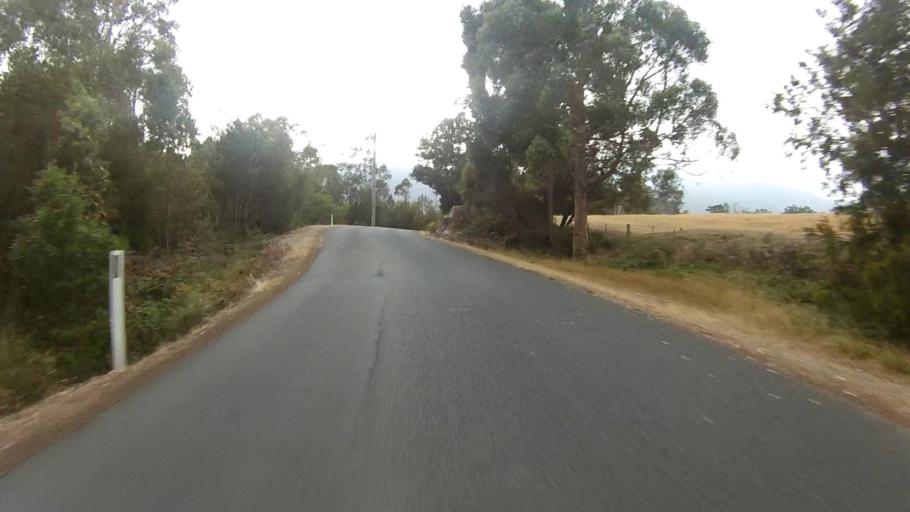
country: AU
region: Tasmania
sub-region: Huon Valley
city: Cygnet
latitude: -43.2154
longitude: 147.1052
